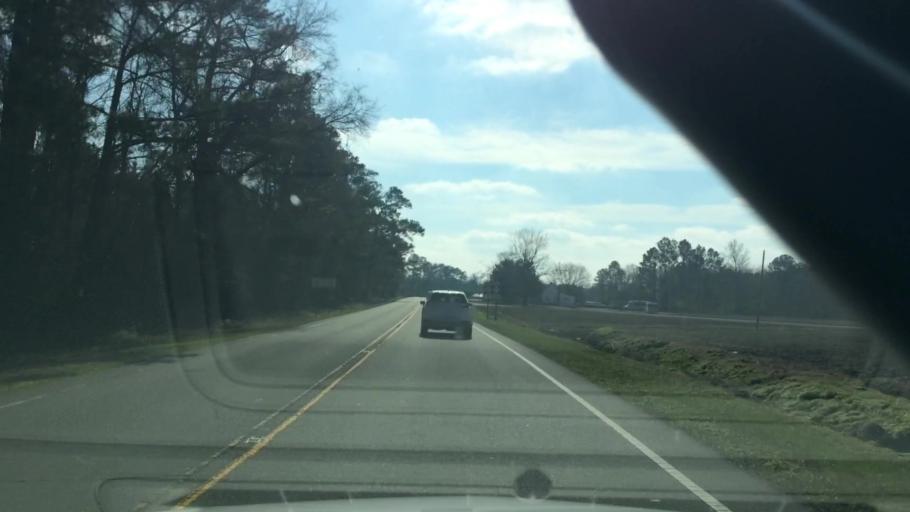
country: US
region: North Carolina
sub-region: Duplin County
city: Beulaville
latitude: 34.8254
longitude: -77.8388
